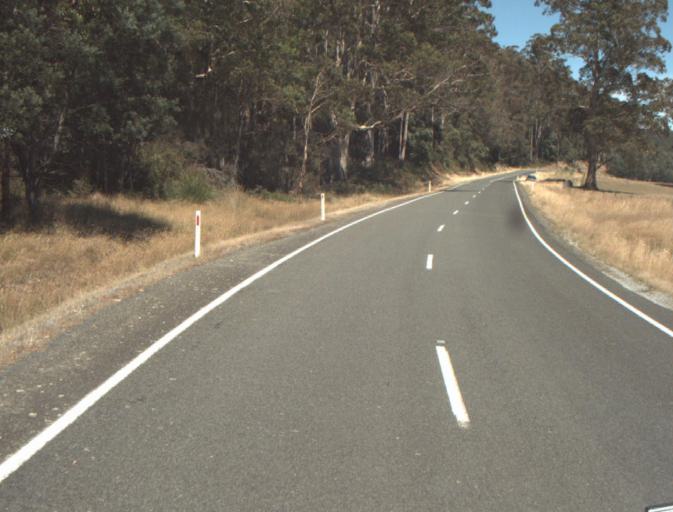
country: AU
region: Tasmania
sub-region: Dorset
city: Scottsdale
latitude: -41.2964
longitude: 147.3850
